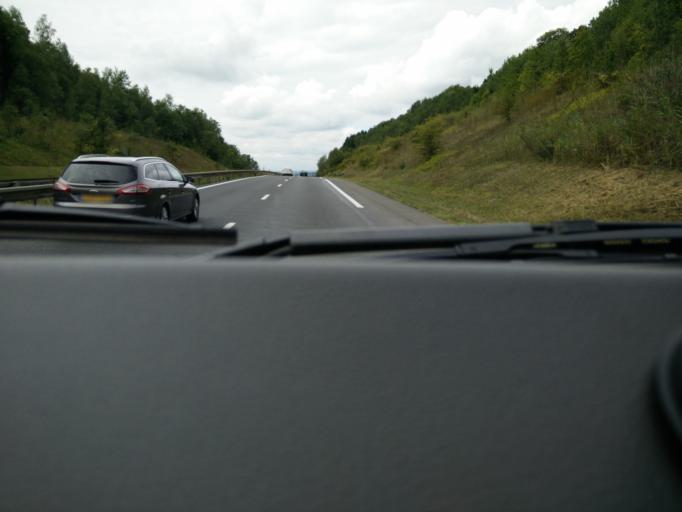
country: FR
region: Champagne-Ardenne
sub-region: Departement des Ardennes
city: Lumes
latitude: 49.7333
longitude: 4.8013
